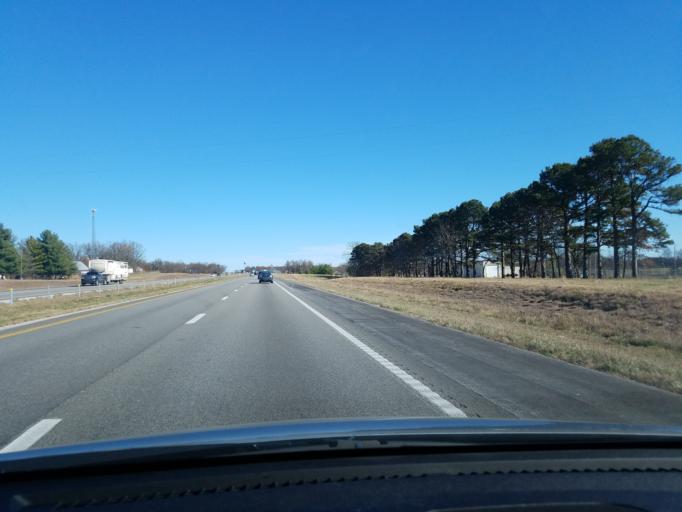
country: US
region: Missouri
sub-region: Greene County
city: Strafford
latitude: 37.2631
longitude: -93.1453
